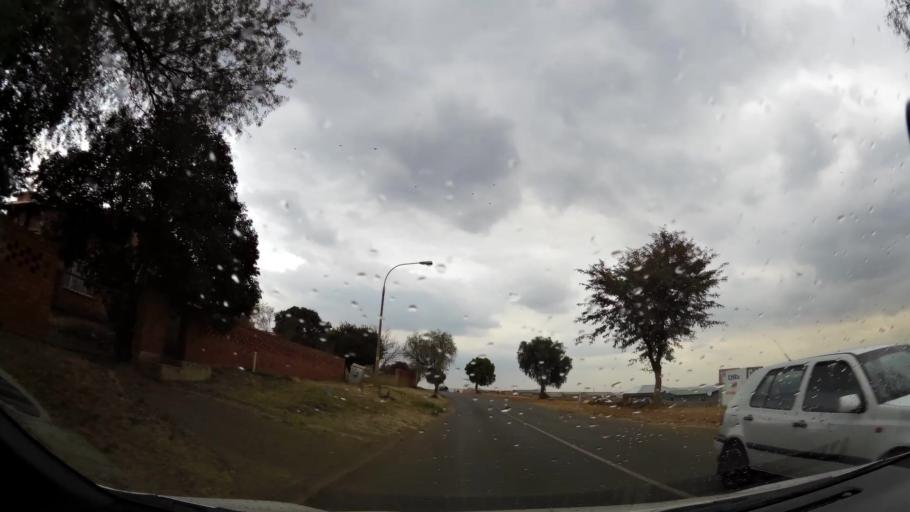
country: ZA
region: Gauteng
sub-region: Ekurhuleni Metropolitan Municipality
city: Germiston
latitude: -26.3763
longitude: 28.1200
